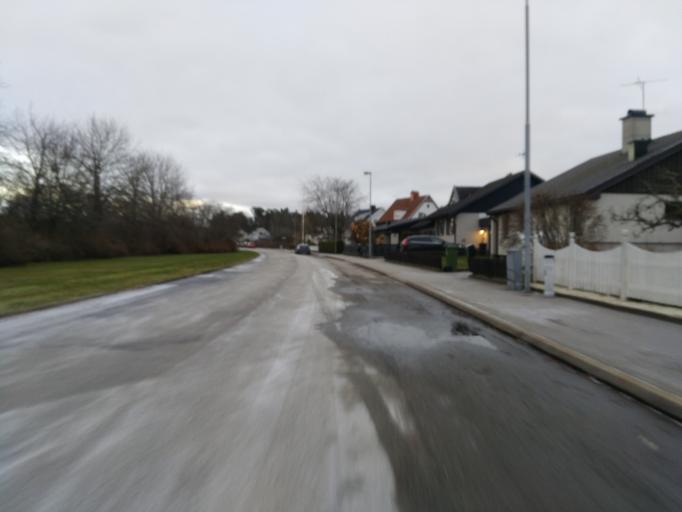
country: SE
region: Vaestra Goetaland
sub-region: Lidkopings Kommun
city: Lidkoping
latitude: 58.4913
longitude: 13.1665
